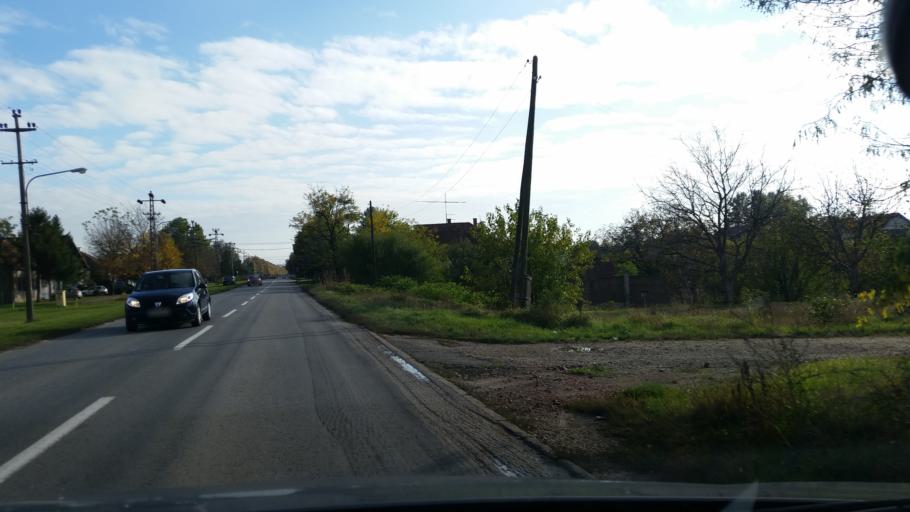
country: RS
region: Autonomna Pokrajina Vojvodina
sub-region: Srednjebanatski Okrug
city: Zrenjanin
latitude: 45.3969
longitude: 20.3781
